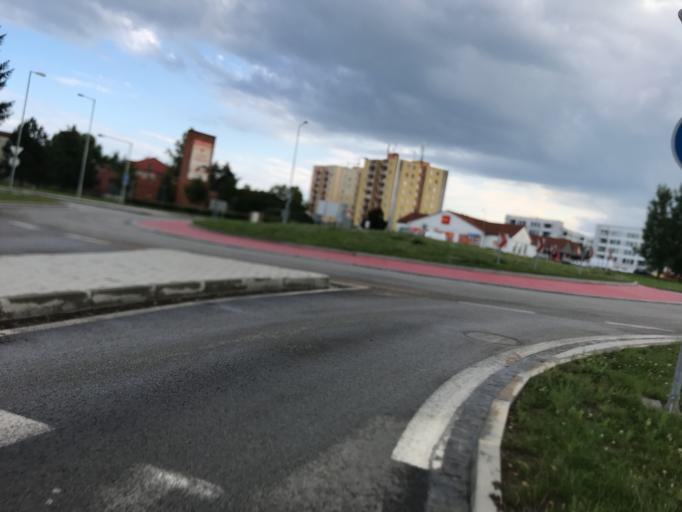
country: CZ
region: Jihocesky
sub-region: Okres Jindrichuv Hradec
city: Trebon
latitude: 49.0135
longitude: 14.7567
